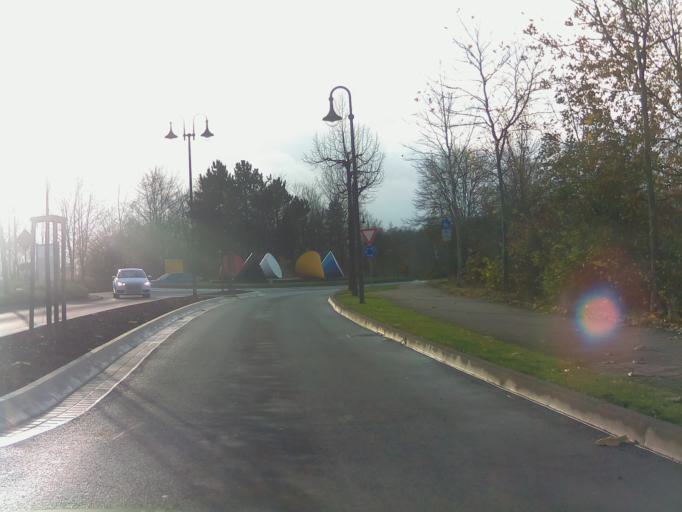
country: DE
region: Hesse
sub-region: Regierungsbezirk Kassel
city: Hunfeld
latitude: 50.6655
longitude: 9.7602
